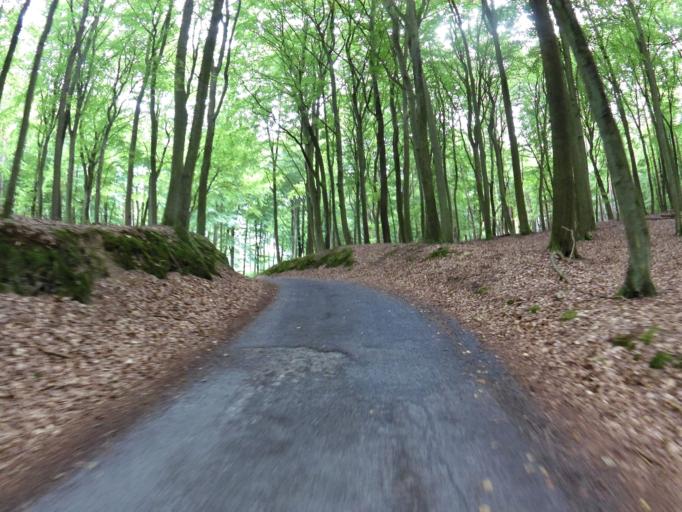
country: DE
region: Mecklenburg-Vorpommern
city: Seebad Heringsdorf
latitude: 53.9256
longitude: 14.1712
